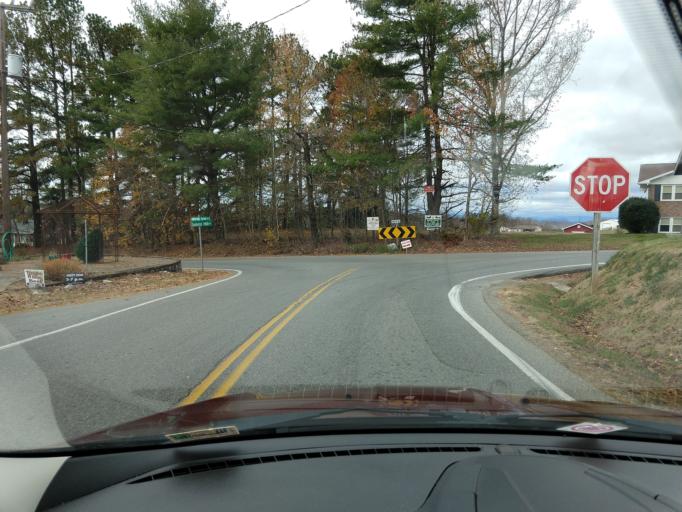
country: US
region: Virginia
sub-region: Franklin County
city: North Shore
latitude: 37.1973
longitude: -79.6854
